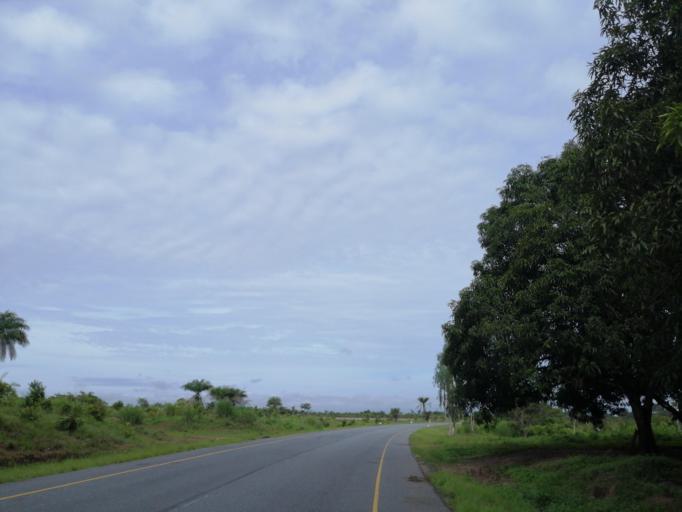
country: SL
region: Northern Province
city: Port Loko
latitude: 8.7702
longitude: -12.8720
